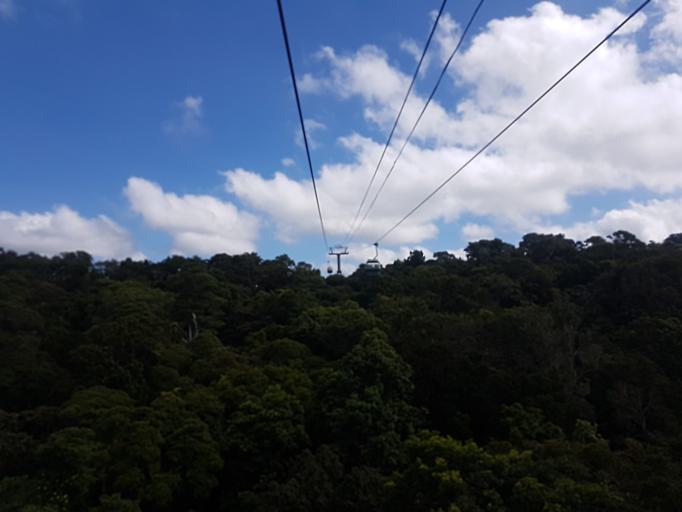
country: AU
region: Queensland
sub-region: Tablelands
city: Kuranda
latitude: -16.8413
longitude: 145.6574
